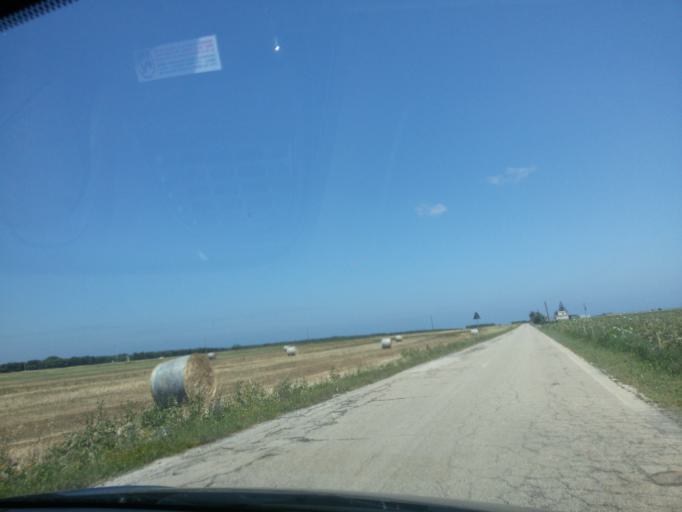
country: IT
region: Apulia
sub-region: Provincia di Brindisi
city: Mesagne
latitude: 40.6525
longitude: 17.8386
